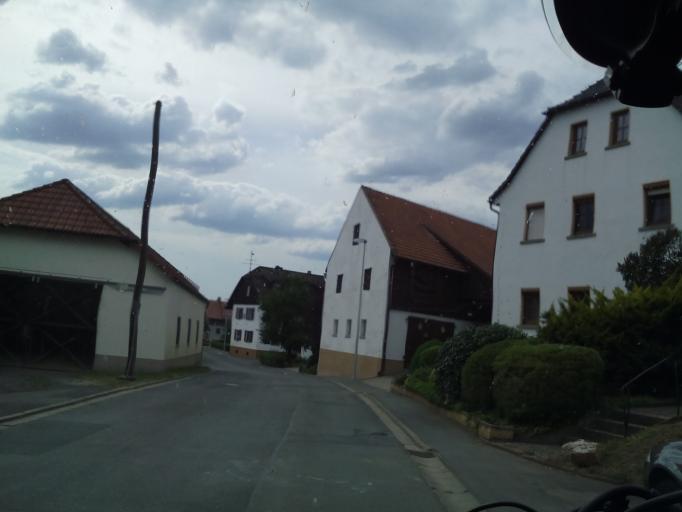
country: DE
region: Bavaria
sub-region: Upper Franconia
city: Sesslach
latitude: 50.1837
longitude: 10.8120
